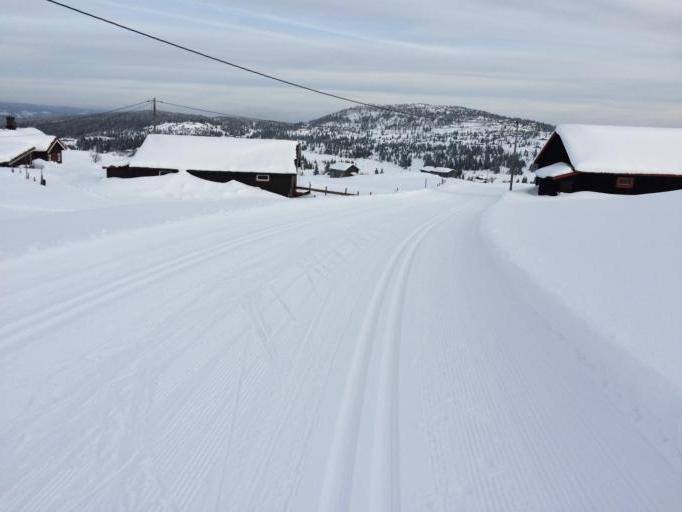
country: NO
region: Oppland
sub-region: Gausdal
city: Segalstad bru
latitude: 61.3152
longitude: 10.0509
